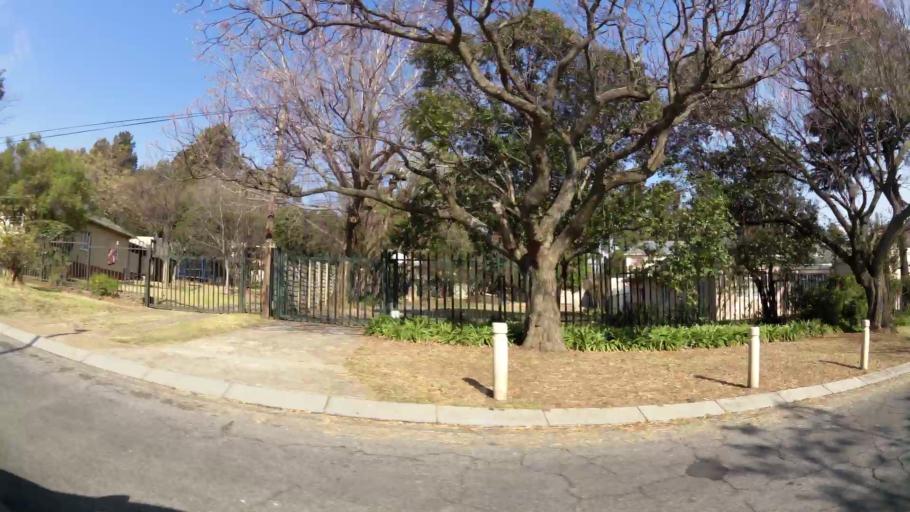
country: ZA
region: Gauteng
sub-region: City of Johannesburg Metropolitan Municipality
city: Modderfontein
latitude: -26.1032
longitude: 28.1536
